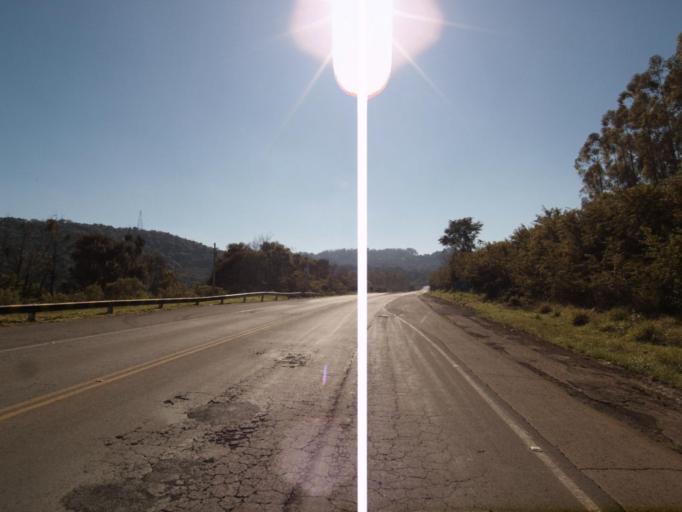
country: BR
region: Rio Grande do Sul
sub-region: Frederico Westphalen
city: Frederico Westphalen
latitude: -27.0724
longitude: -53.2312
